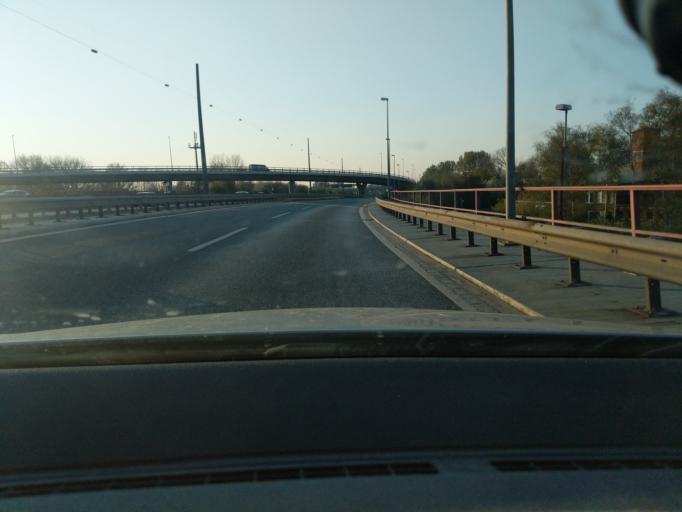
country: DE
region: Hamburg
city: Rothenburgsort
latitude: 53.5167
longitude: 10.0302
